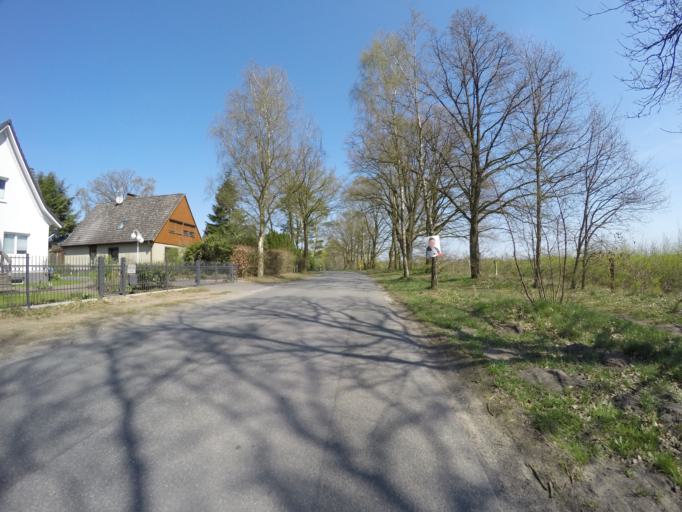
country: DE
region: Schleswig-Holstein
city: Quickborn
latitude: 53.7224
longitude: 9.9258
